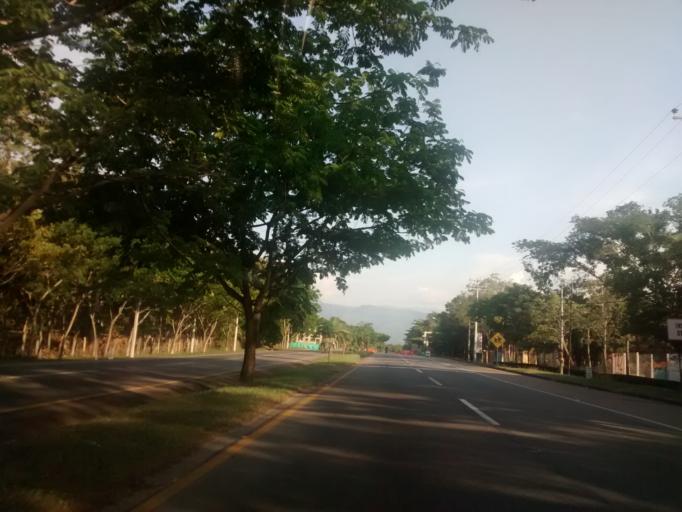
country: CO
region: Tolima
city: Melgar
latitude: 4.2251
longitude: -74.6978
